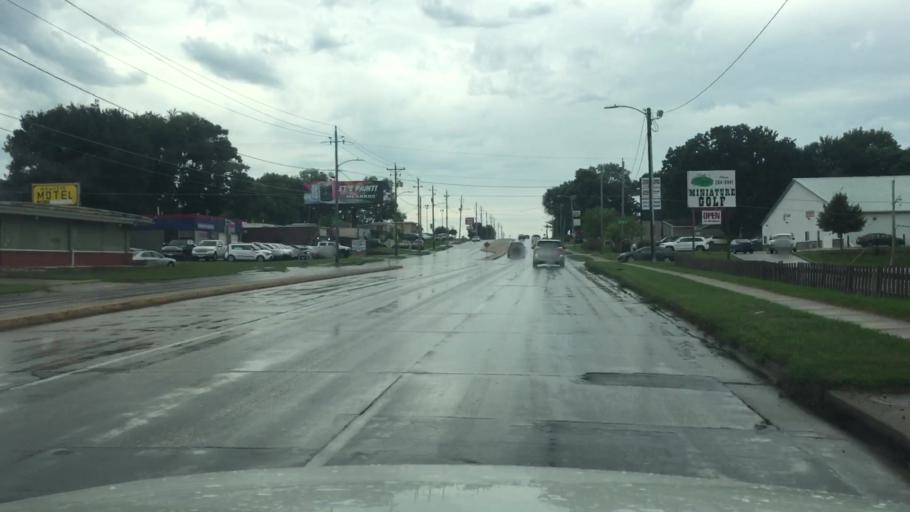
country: US
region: Iowa
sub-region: Polk County
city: Des Moines
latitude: 41.5607
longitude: -93.5970
